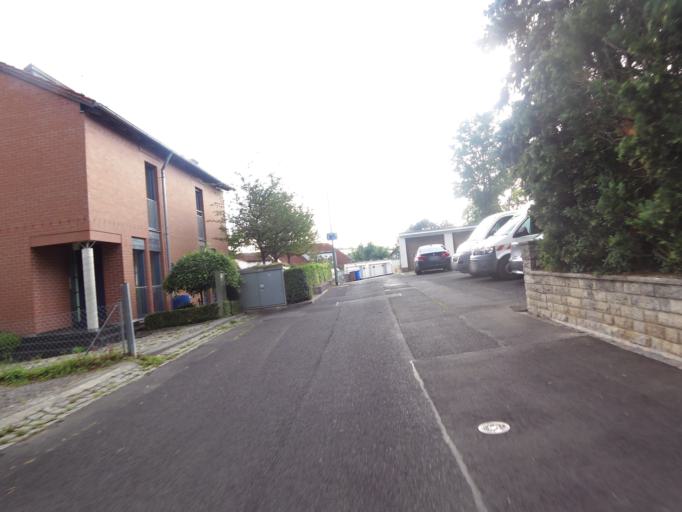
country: DE
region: Bavaria
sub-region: Regierungsbezirk Unterfranken
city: Wuerzburg
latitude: 49.8146
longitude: 9.9677
